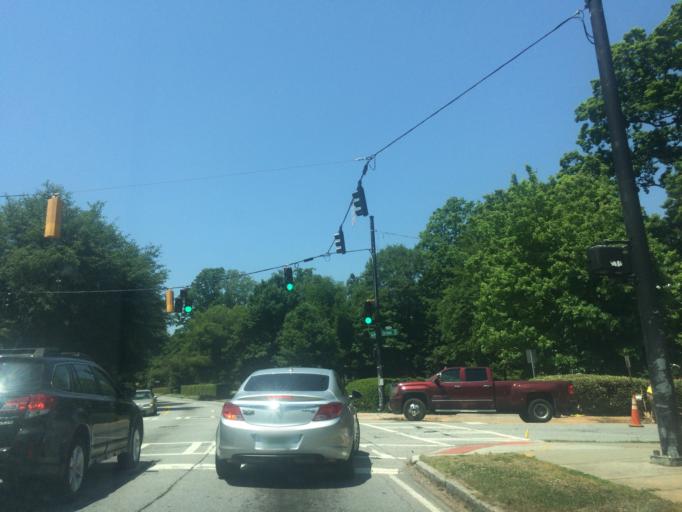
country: US
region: Georgia
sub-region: DeKalb County
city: Druid Hills
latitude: 33.7752
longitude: -84.3412
